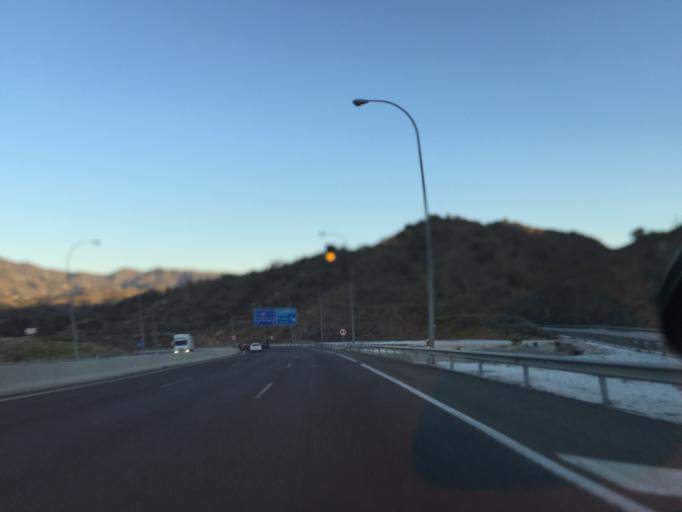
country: ES
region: Andalusia
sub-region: Provincia de Malaga
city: Malaga
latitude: 36.7535
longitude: -4.4155
